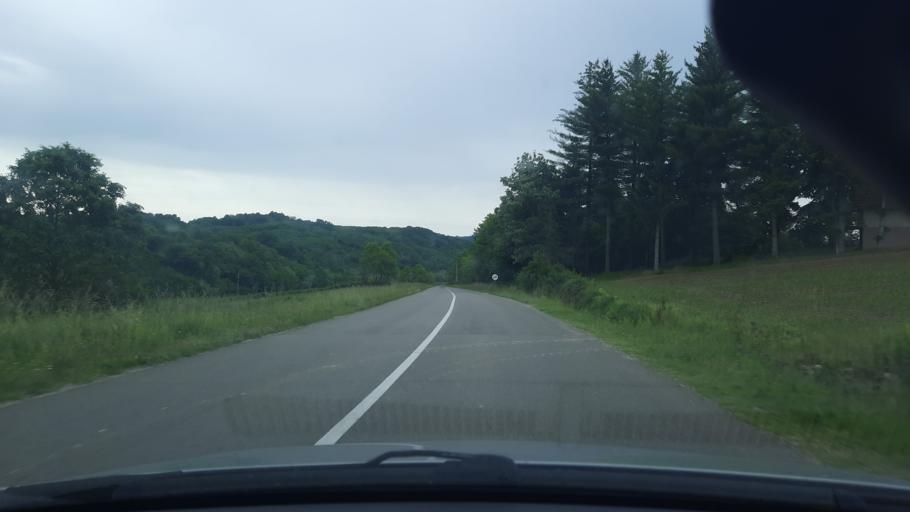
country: RS
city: Bukor
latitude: 44.5334
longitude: 19.5134
